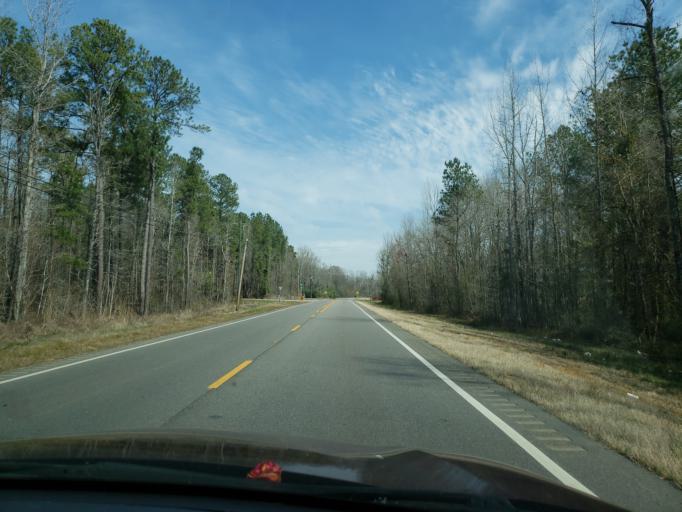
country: US
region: Alabama
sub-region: Elmore County
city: Eclectic
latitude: 32.5788
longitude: -86.0924
